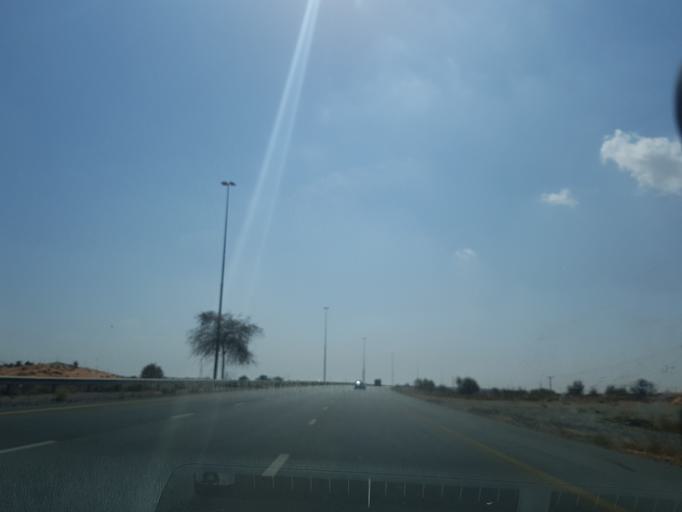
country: AE
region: Ra's al Khaymah
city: Ras al-Khaimah
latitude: 25.6830
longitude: 55.8831
